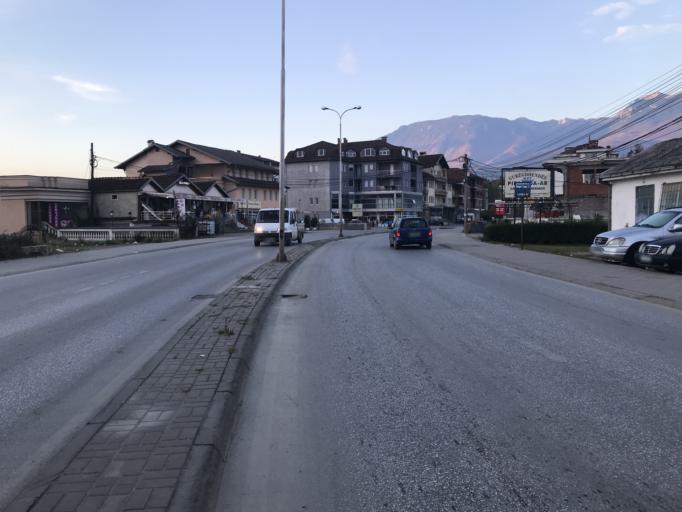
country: XK
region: Pec
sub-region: Komuna e Pejes
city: Peje
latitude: 42.6707
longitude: 20.3090
